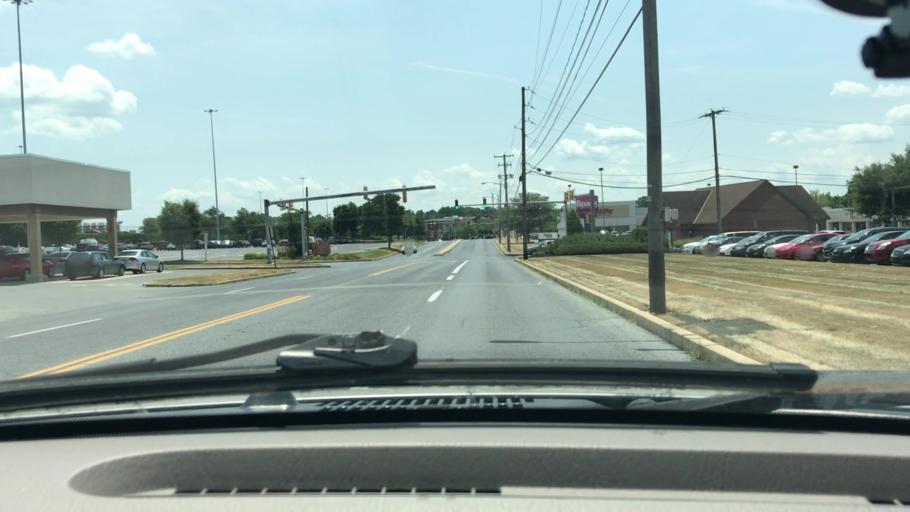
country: US
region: Pennsylvania
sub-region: Lancaster County
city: East Petersburg
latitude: 40.0694
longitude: -76.3427
